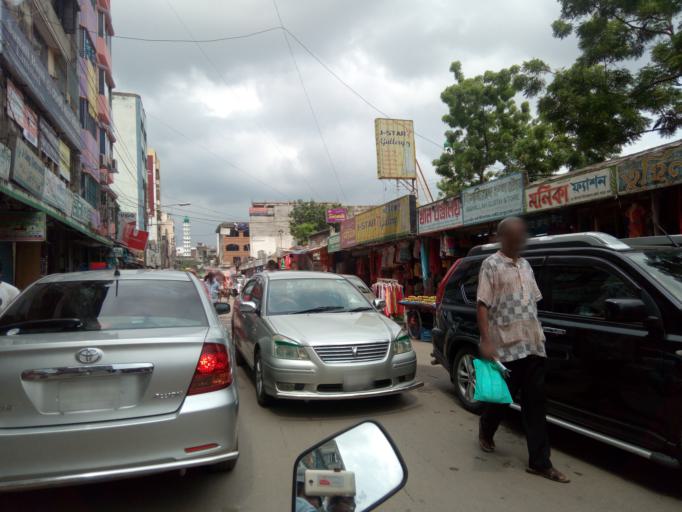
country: BD
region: Dhaka
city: Azimpur
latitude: 23.7598
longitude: 90.3647
